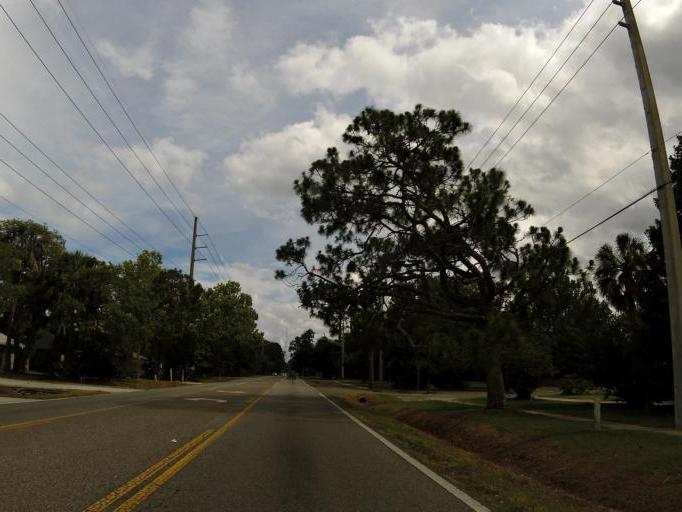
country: US
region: Florida
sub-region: Duval County
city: Jacksonville Beach
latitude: 30.2941
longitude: -81.4064
